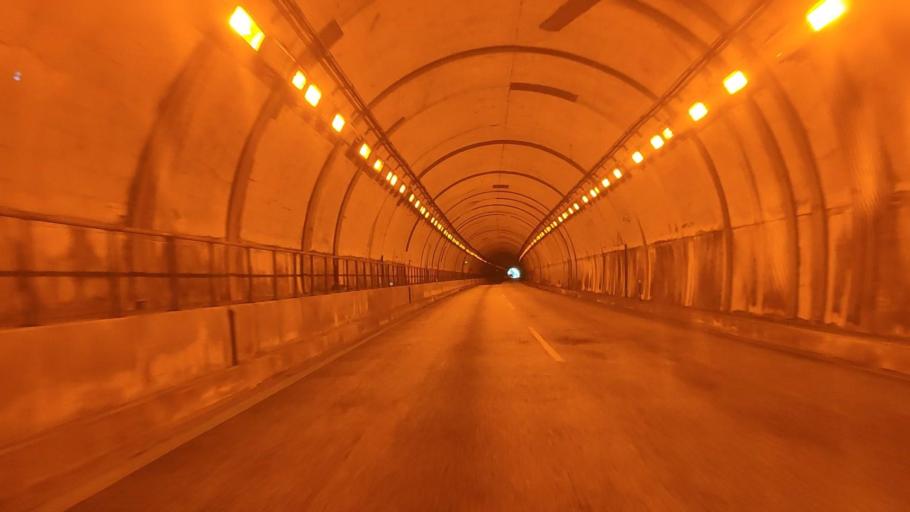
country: JP
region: Miyazaki
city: Miyazaki-shi
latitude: 31.8210
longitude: 131.2567
